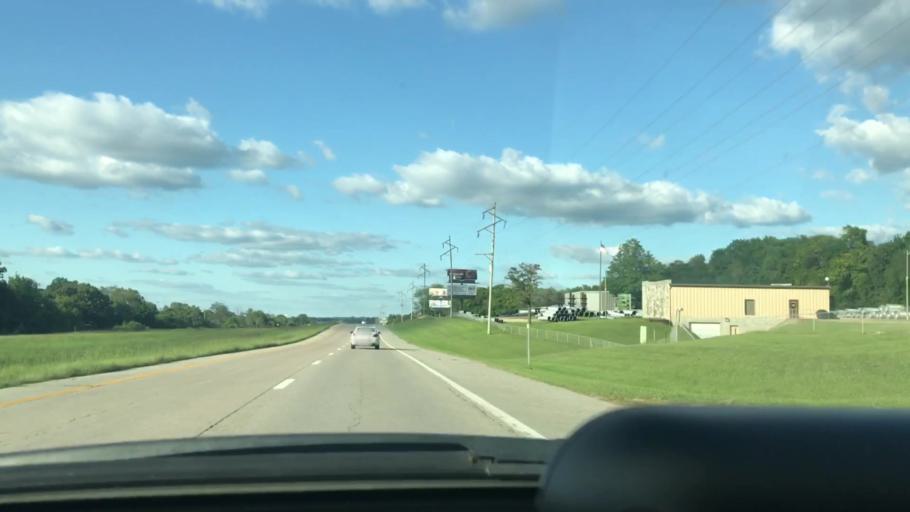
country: US
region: Missouri
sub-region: Pettis County
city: Sedalia
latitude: 38.6404
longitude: -93.2645
